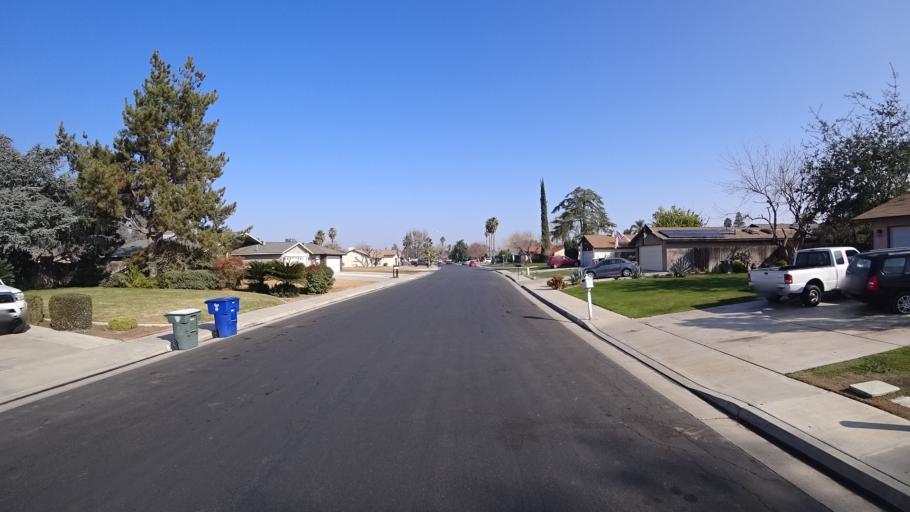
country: US
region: California
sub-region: Kern County
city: Bakersfield
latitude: 35.3210
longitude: -119.0691
